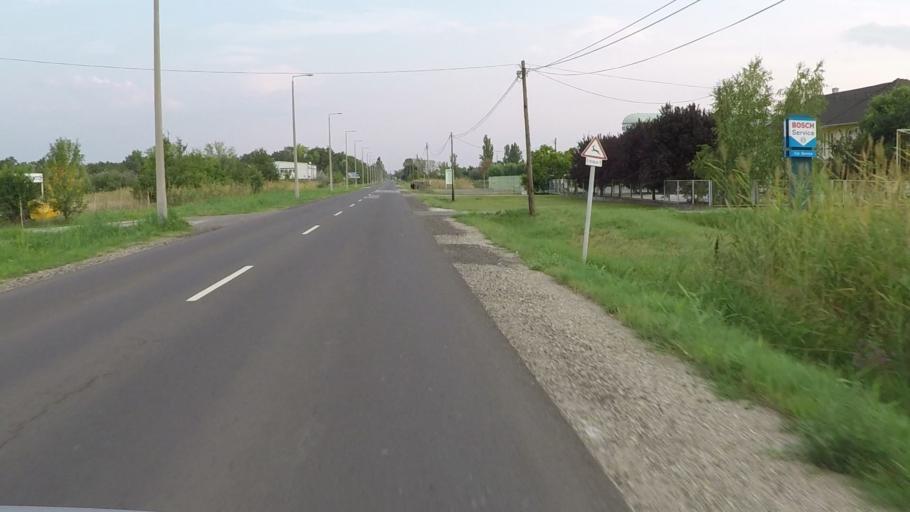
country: HU
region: Jasz-Nagykun-Szolnok
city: Szolnok
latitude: 47.1958
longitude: 20.1579
